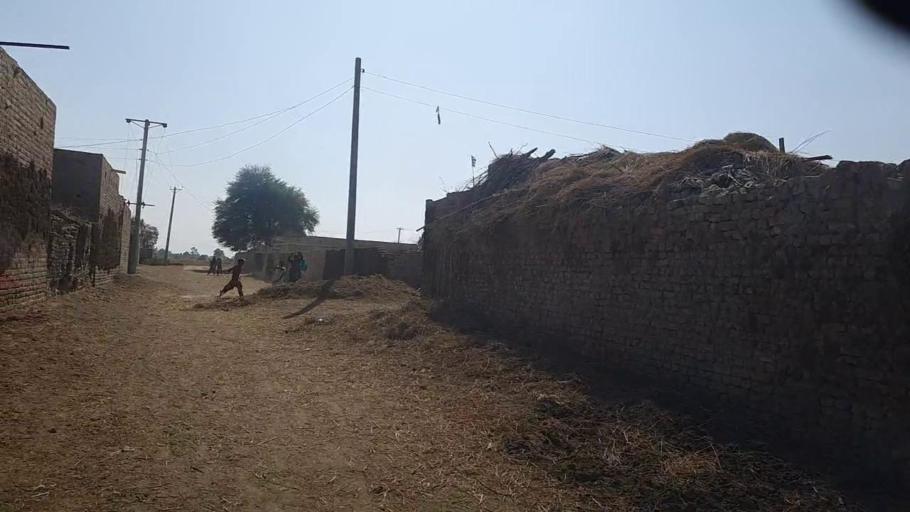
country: PK
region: Sindh
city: Thul
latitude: 28.1723
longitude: 68.7691
